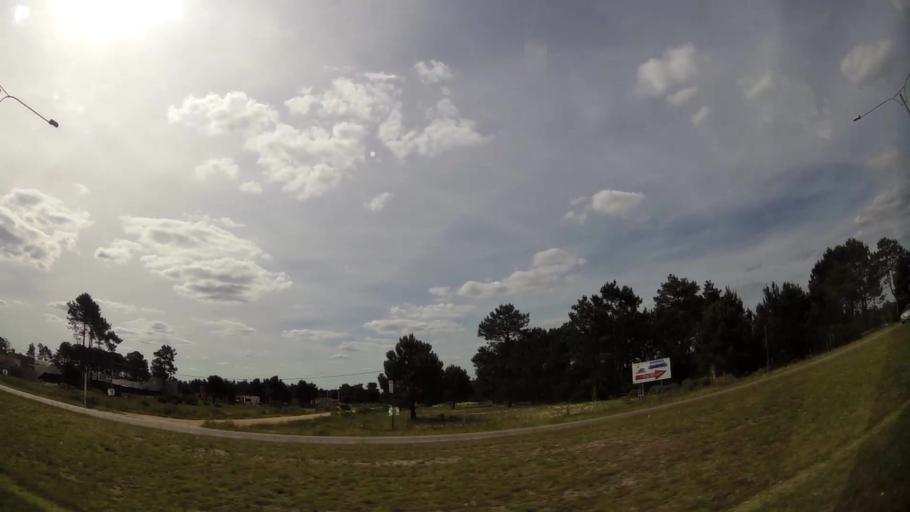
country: UY
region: Canelones
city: Pando
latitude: -34.7953
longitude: -55.9064
